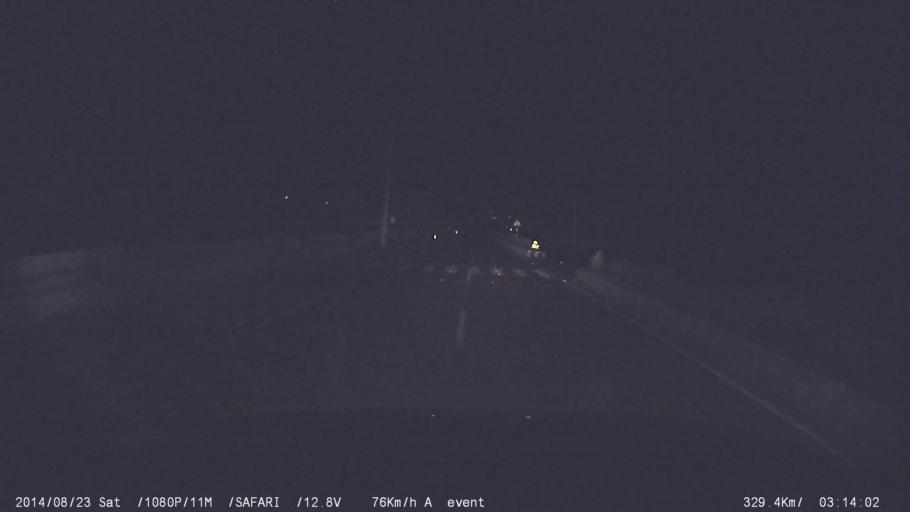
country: IN
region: Tamil Nadu
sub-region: Kancheepuram
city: Vengavasal
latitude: 12.8086
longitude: 80.1865
